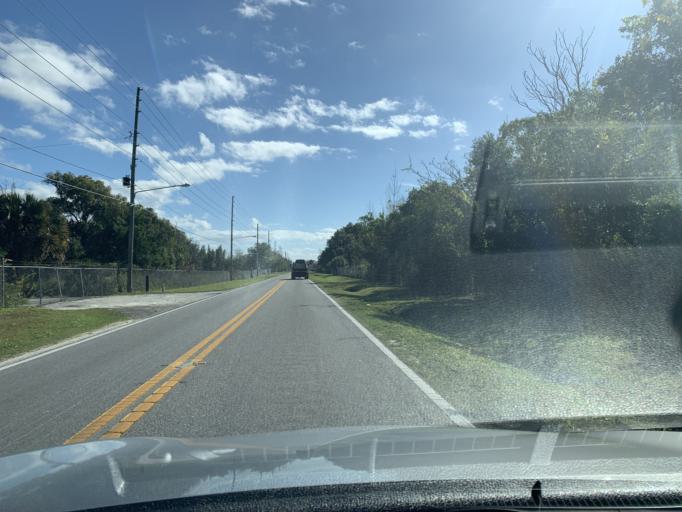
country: US
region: Florida
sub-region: Seminole County
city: Forest City
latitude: 28.6432
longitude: -81.4650
